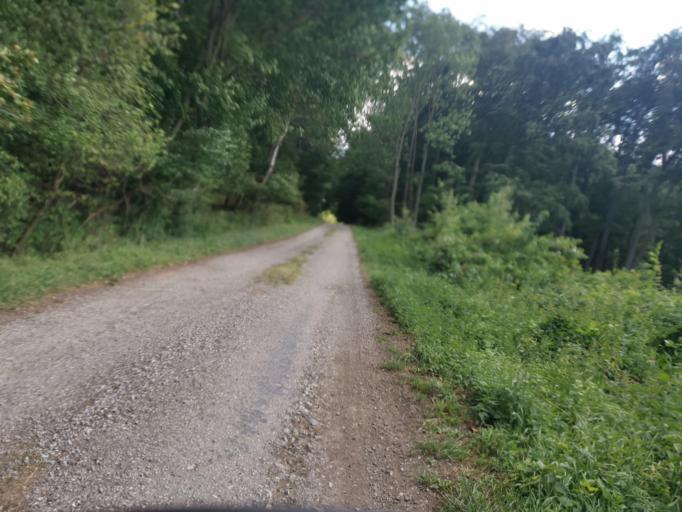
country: CZ
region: South Moravian
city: Knezdub
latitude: 48.8172
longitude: 17.4178
